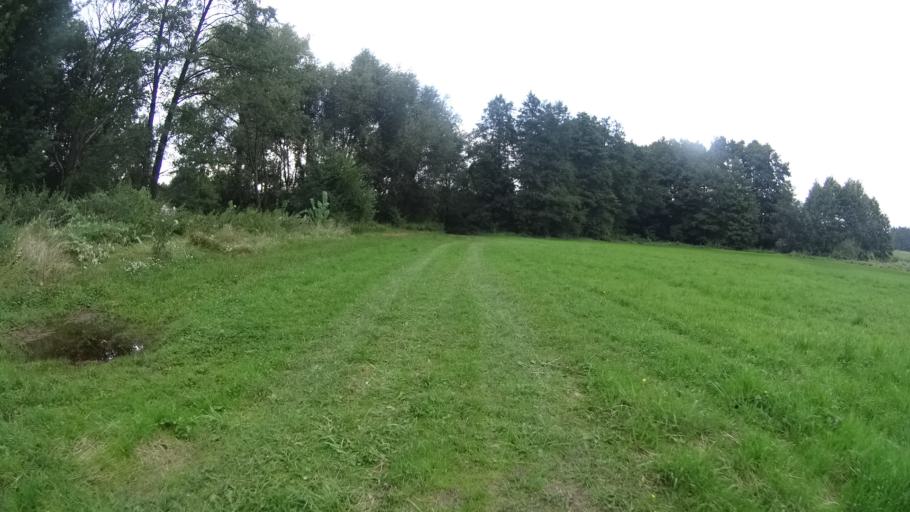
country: PL
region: Masovian Voivodeship
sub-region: Powiat grojecki
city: Mogielnica
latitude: 51.6690
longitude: 20.7444
